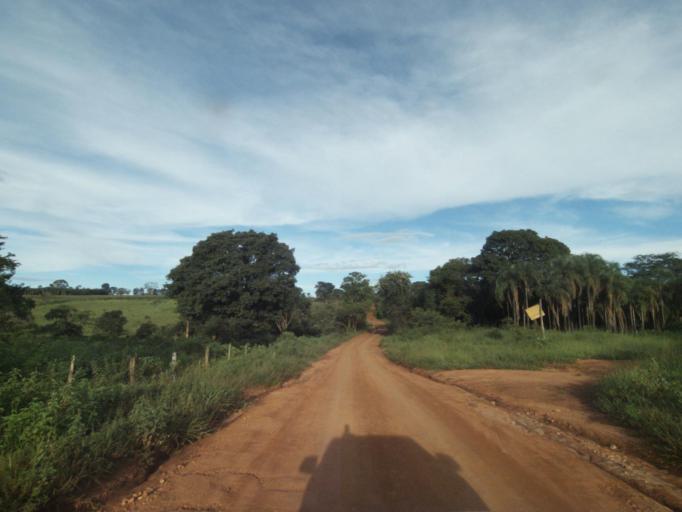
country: BR
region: Goias
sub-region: Jaragua
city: Jaragua
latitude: -15.8895
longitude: -49.4755
